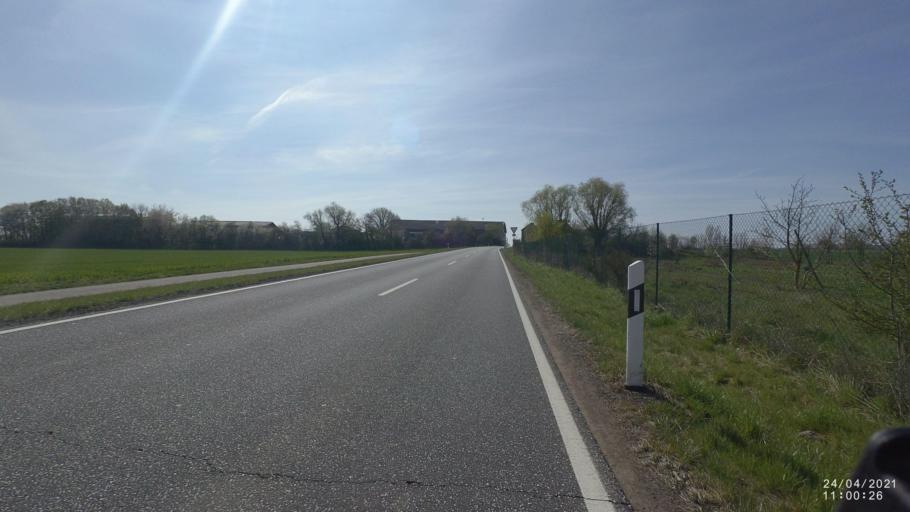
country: DE
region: Rheinland-Pfalz
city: Welling
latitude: 50.3365
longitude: 7.3031
